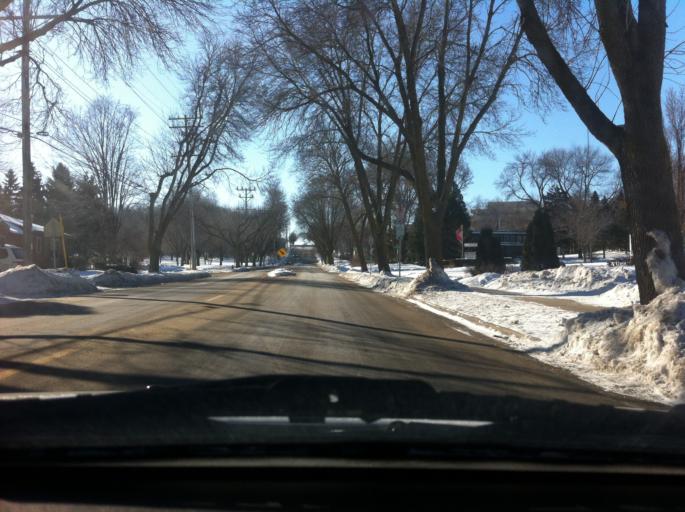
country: US
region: Wisconsin
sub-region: Dane County
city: Shorewood Hills
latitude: 43.0652
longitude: -89.4785
